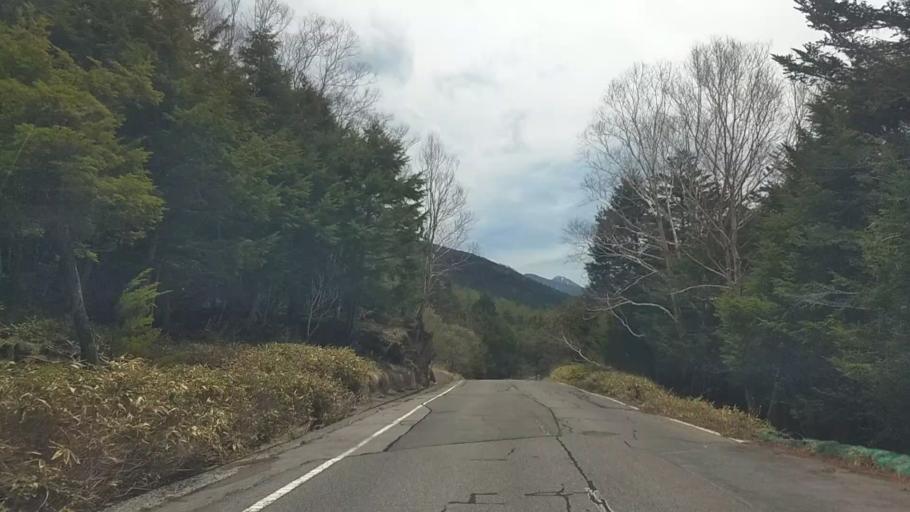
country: JP
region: Nagano
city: Chino
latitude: 36.0544
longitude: 138.3193
